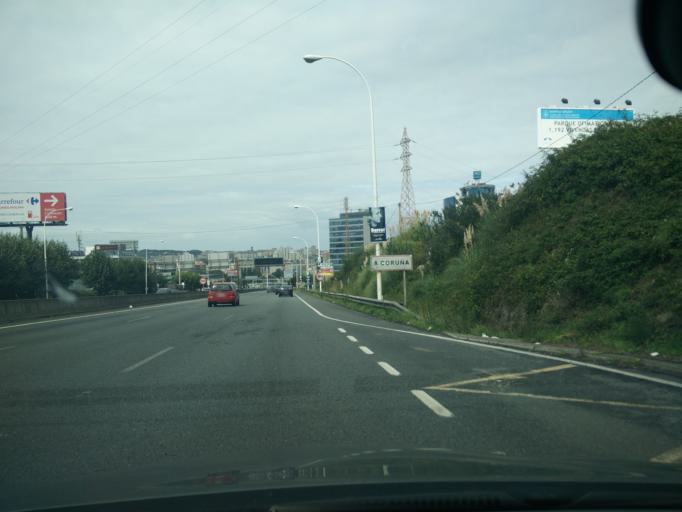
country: ES
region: Galicia
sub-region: Provincia da Coruna
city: A Coruna
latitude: 43.3359
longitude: -8.4034
